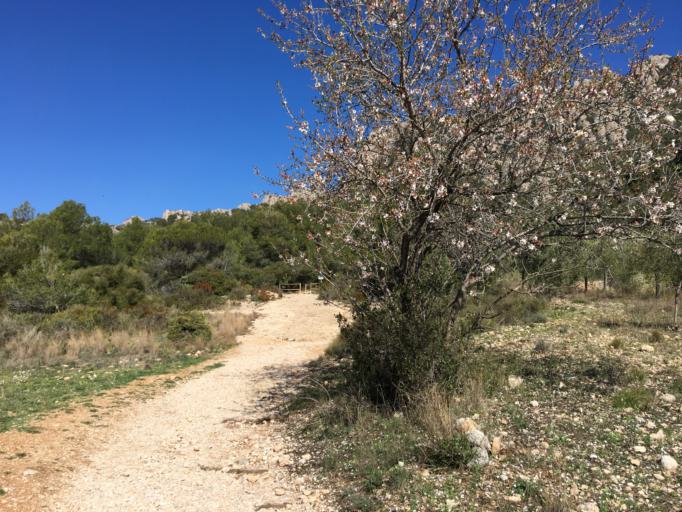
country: ES
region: Catalonia
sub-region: Provincia de Barcelona
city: Collbato
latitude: 41.5749
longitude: 1.8200
